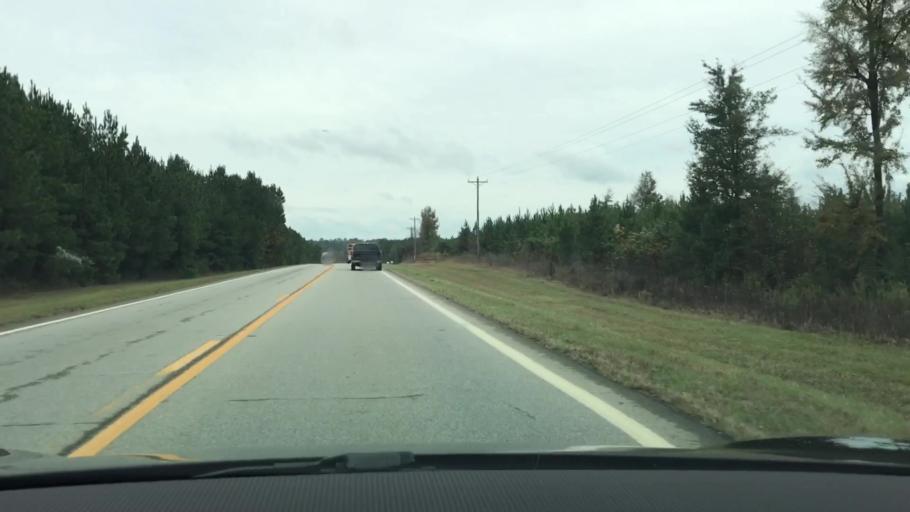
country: US
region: Georgia
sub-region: Greene County
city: Greensboro
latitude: 33.5988
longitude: -83.1968
